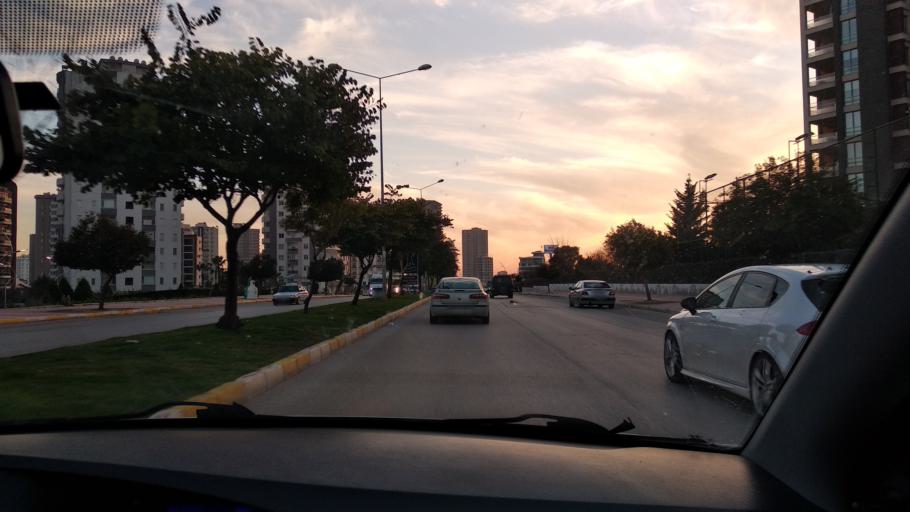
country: TR
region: Mersin
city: Mercin
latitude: 36.8052
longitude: 34.5865
